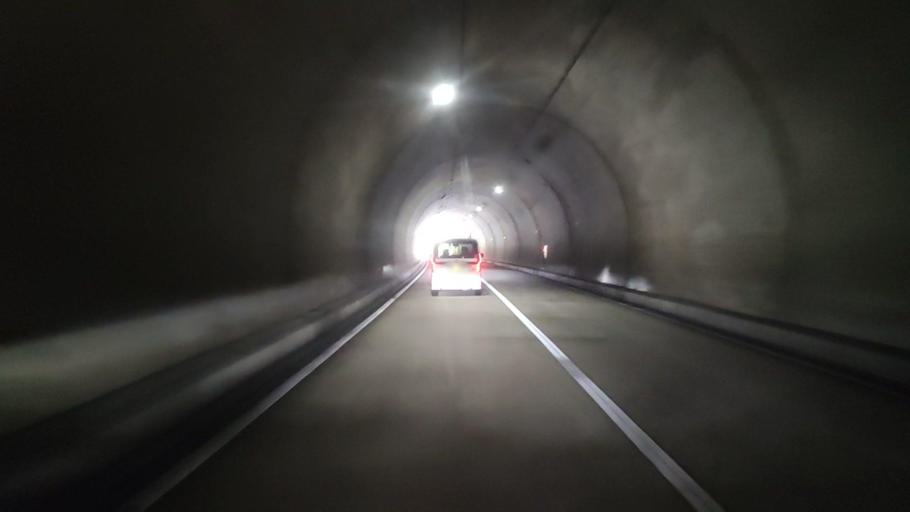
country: JP
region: Wakayama
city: Shingu
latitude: 33.8877
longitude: 135.8796
